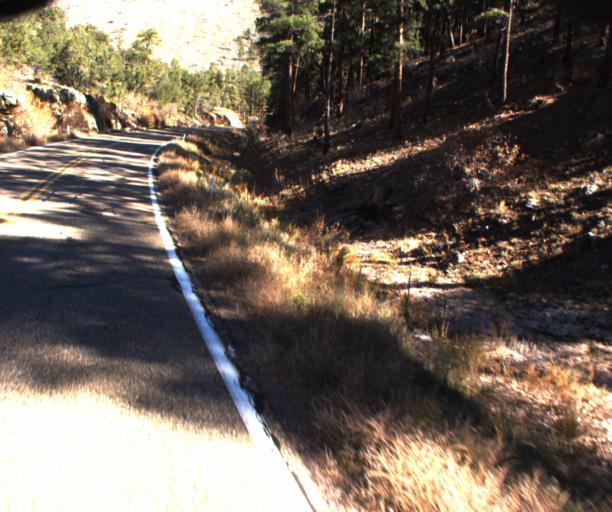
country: US
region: Arizona
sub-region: Coconino County
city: Fredonia
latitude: 36.7338
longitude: -112.1345
